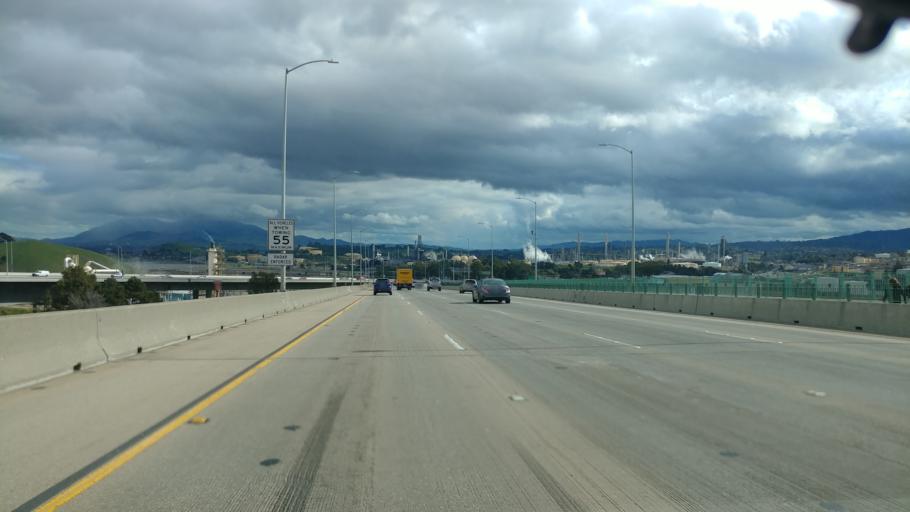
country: US
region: California
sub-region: Contra Costa County
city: Martinez
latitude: 38.0364
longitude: -122.1199
